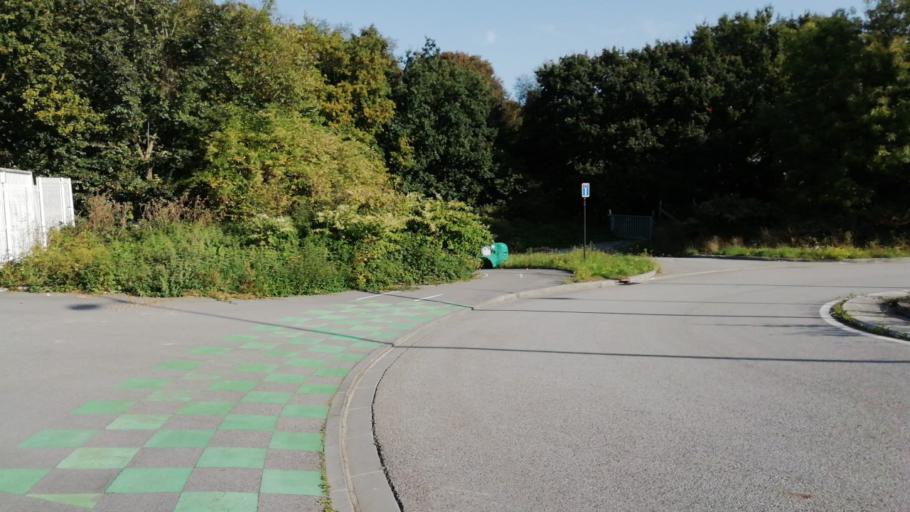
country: FR
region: Haute-Normandie
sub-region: Departement de la Seine-Maritime
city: Harfleur
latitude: 49.5160
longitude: 0.2069
